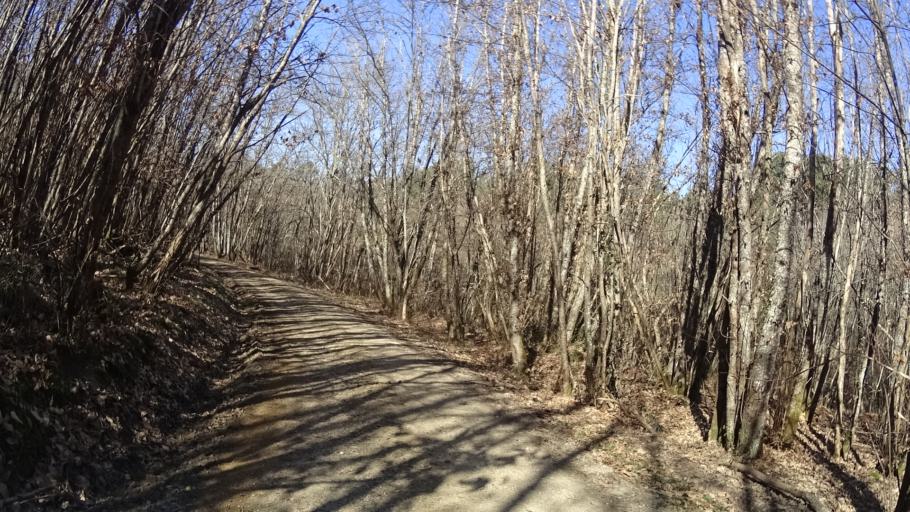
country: FR
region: Aquitaine
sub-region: Departement de la Dordogne
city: Riberac
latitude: 45.1953
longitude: 0.3170
